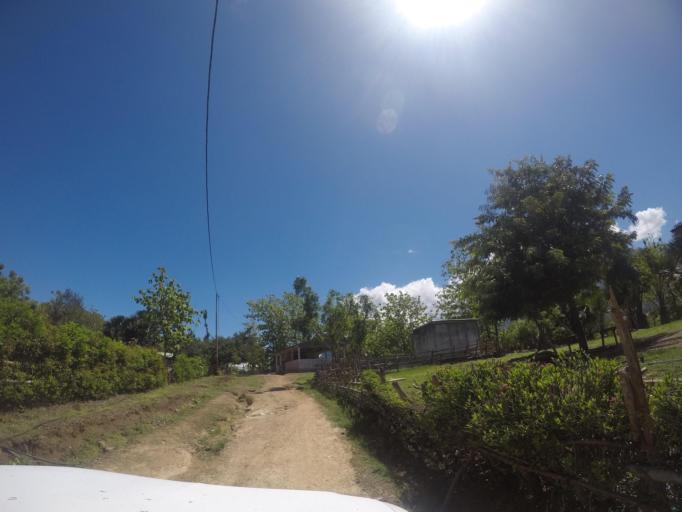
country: TL
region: Bobonaro
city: Maliana
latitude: -8.9663
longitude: 125.2100
